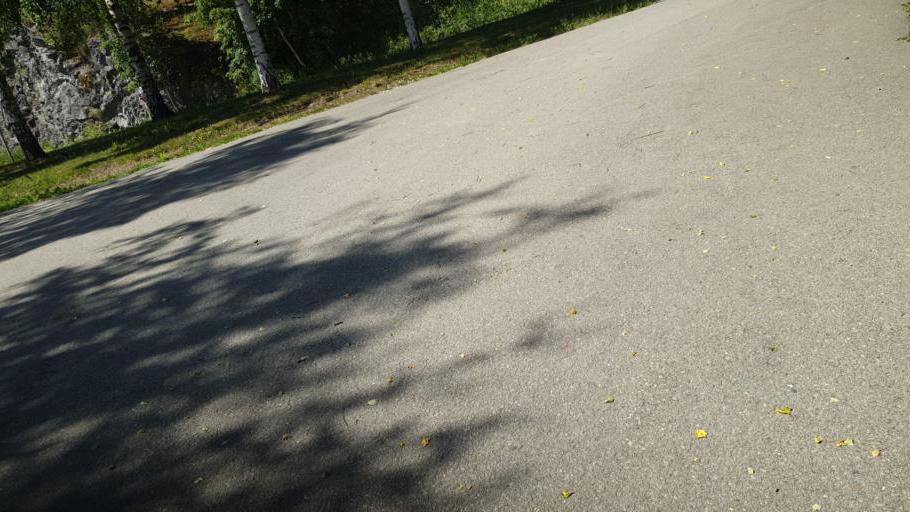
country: NO
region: Sor-Trondelag
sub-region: Trondheim
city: Trondheim
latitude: 63.5534
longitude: 10.2221
